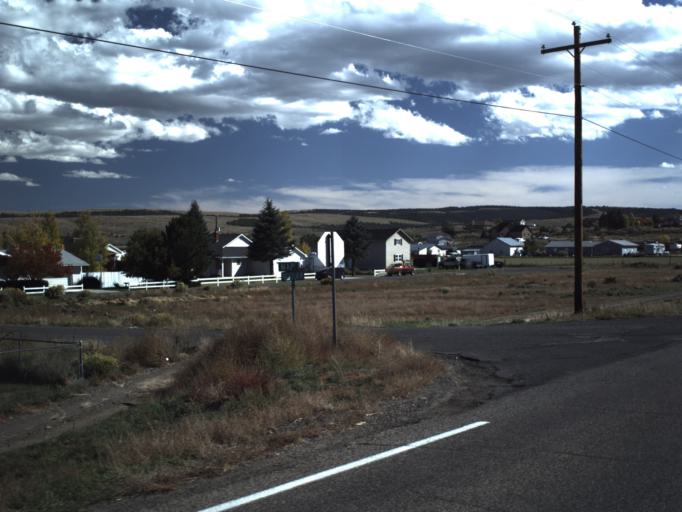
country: US
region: Utah
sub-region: Garfield County
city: Panguitch
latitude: 37.8126
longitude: -112.4355
